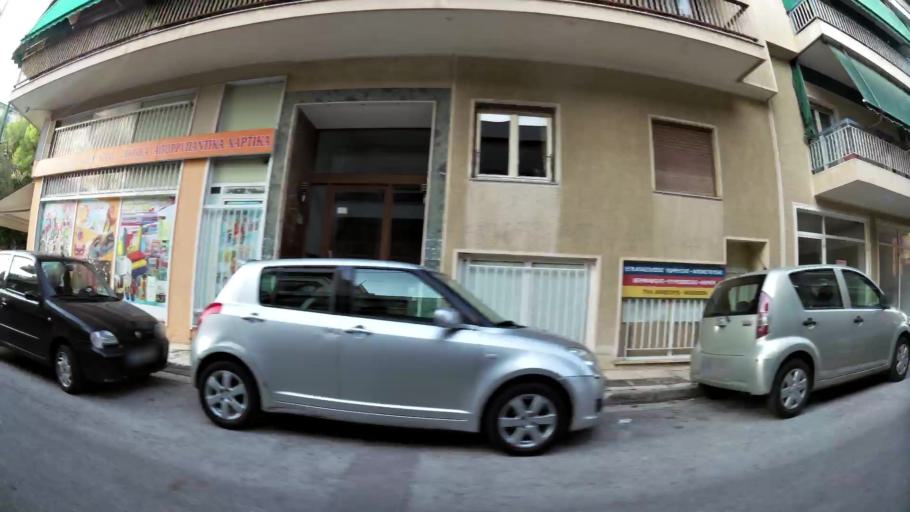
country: GR
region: Attica
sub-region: Nomarchia Athinas
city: Galatsi
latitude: 38.0241
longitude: 23.7536
